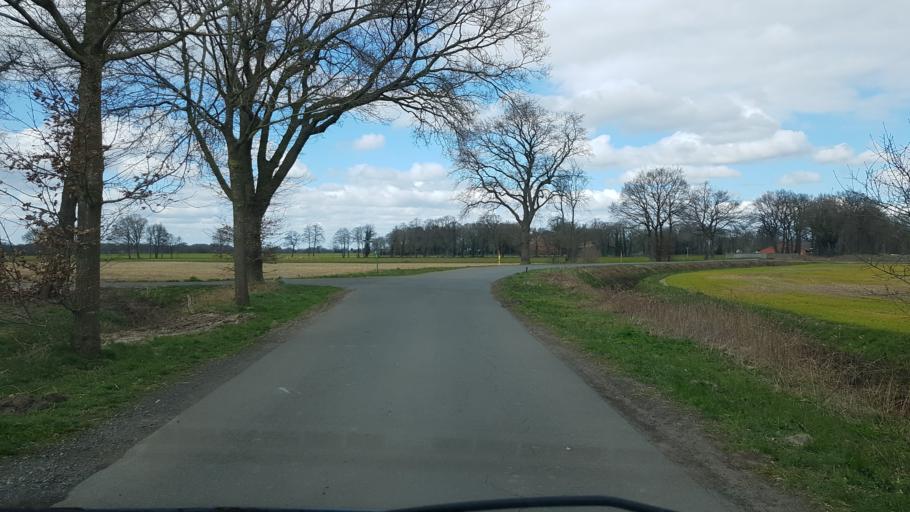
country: DE
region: Lower Saxony
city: Edewecht
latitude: 53.1095
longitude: 7.9425
